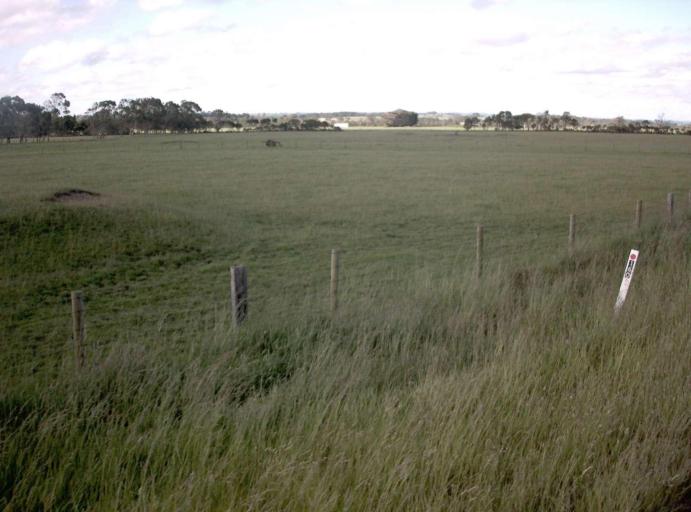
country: AU
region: Victoria
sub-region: Bass Coast
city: North Wonthaggi
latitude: -38.5335
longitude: 145.8739
